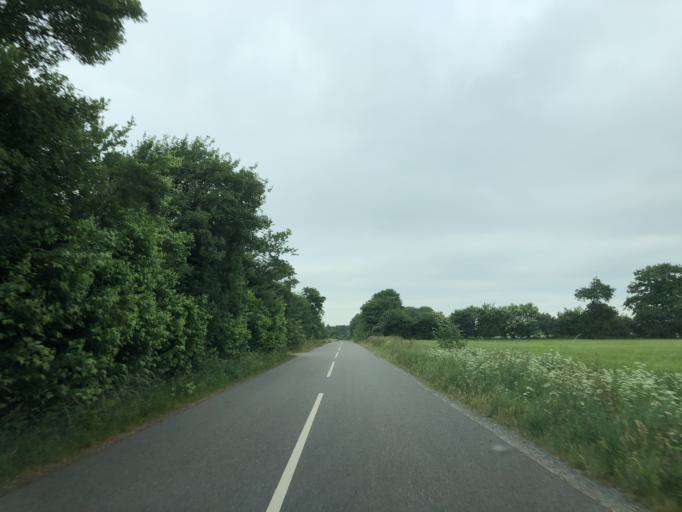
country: DK
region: Central Jutland
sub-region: Holstebro Kommune
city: Holstebro
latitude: 56.2456
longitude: 8.6238
